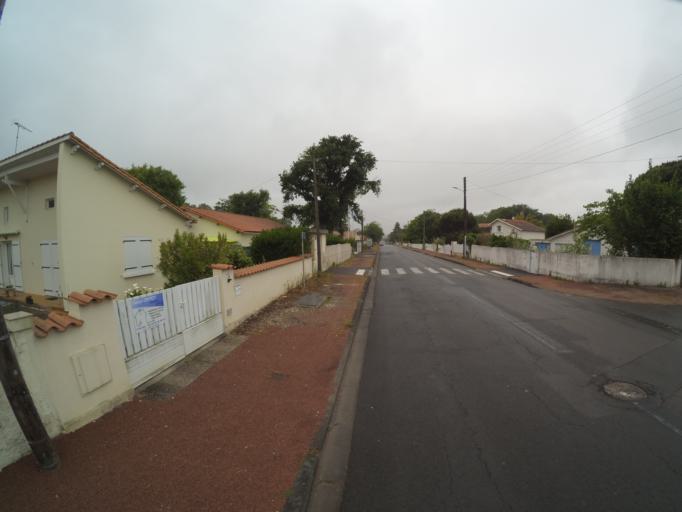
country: FR
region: Poitou-Charentes
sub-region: Departement de la Charente-Maritime
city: Saint-Georges-de-Didonne
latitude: 45.6100
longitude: -0.9959
